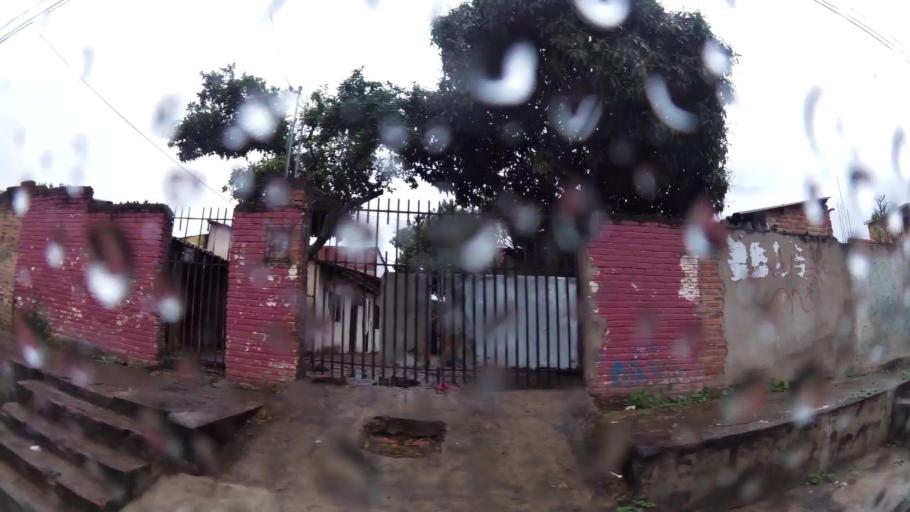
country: BO
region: Santa Cruz
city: Santa Cruz de la Sierra
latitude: -17.7945
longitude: -63.2116
